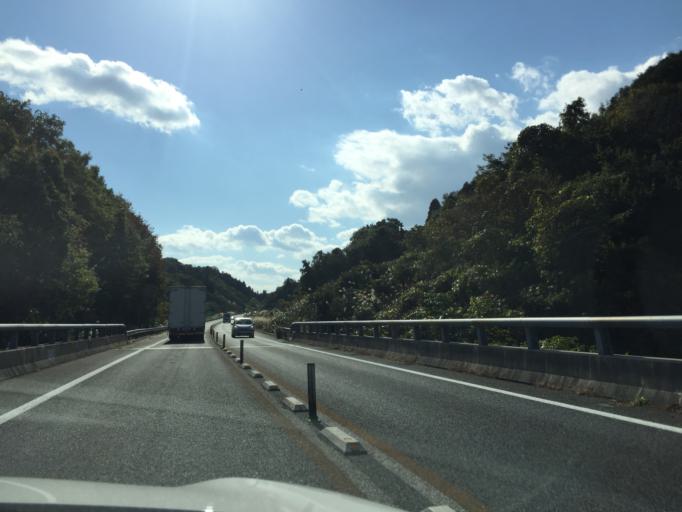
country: JP
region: Fukushima
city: Iwaki
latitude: 37.1451
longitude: 140.9642
